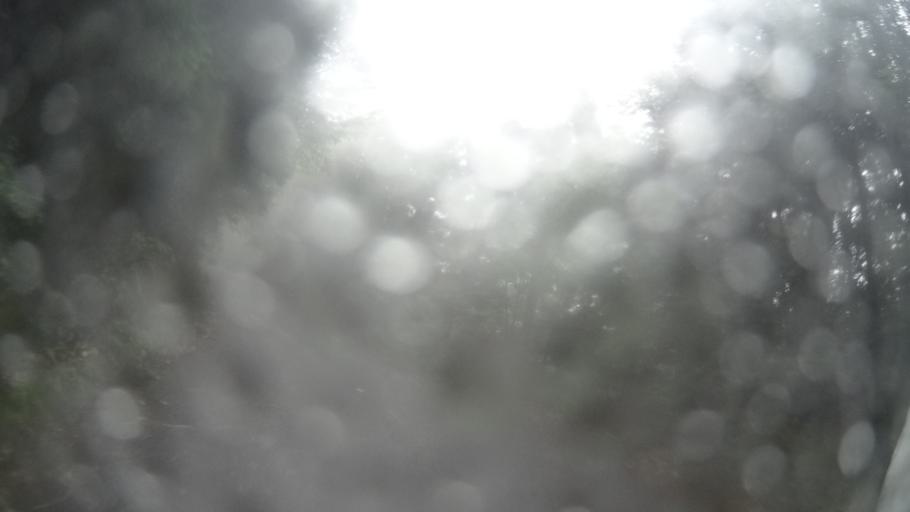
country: JP
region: Kagoshima
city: Nishinoomote
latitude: 30.3027
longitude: 130.5489
